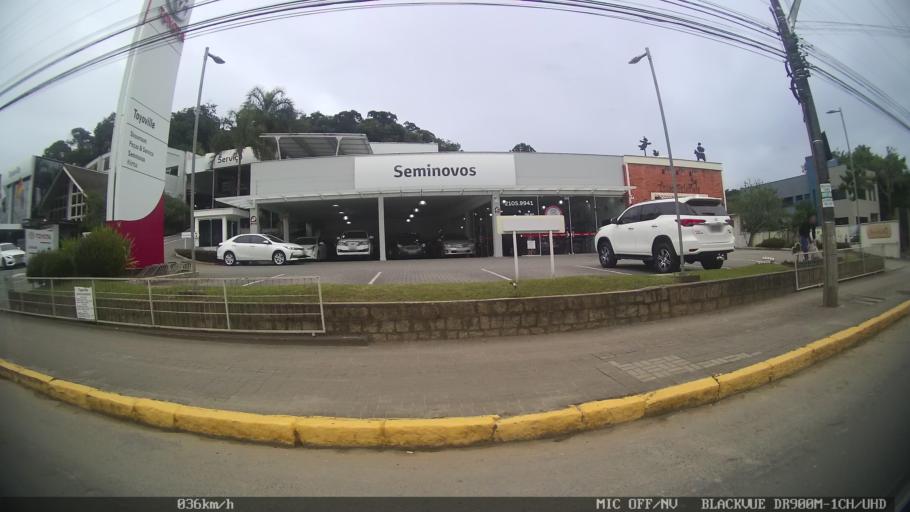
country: BR
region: Santa Catarina
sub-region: Joinville
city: Joinville
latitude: -26.2951
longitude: -48.8810
